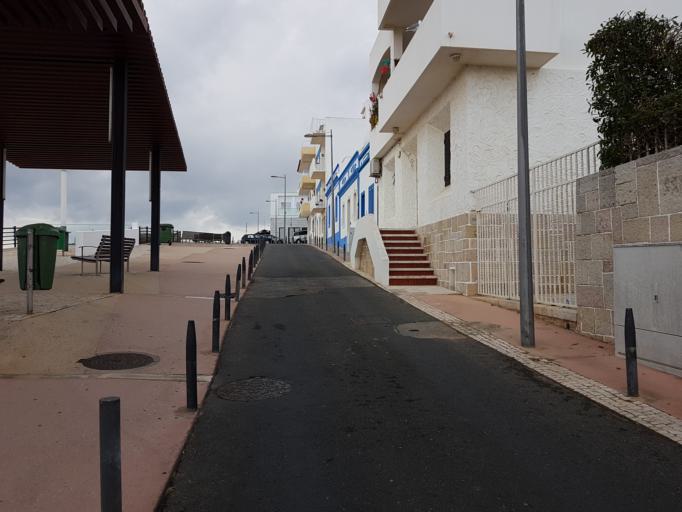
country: PT
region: Faro
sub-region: Albufeira
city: Albufeira
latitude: 37.0864
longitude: -8.2454
